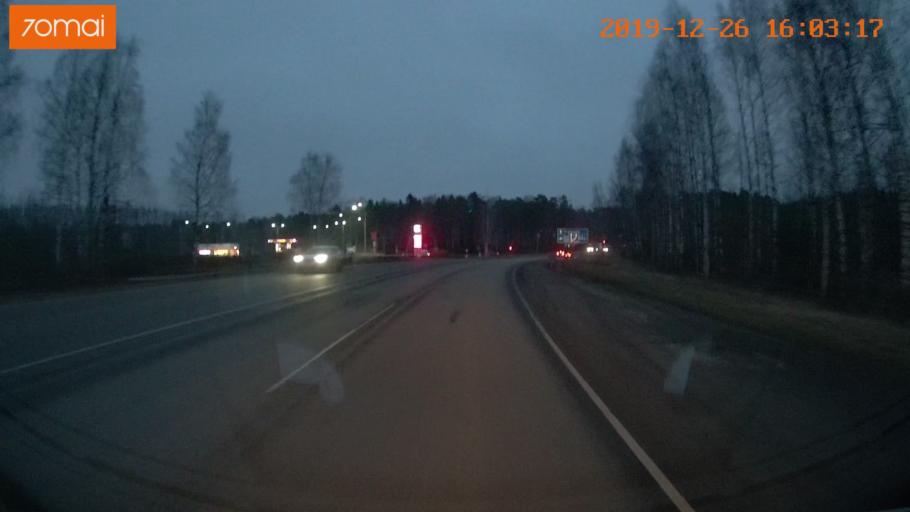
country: RU
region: Jaroslavl
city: Rybinsk
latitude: 58.0110
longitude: 38.8555
